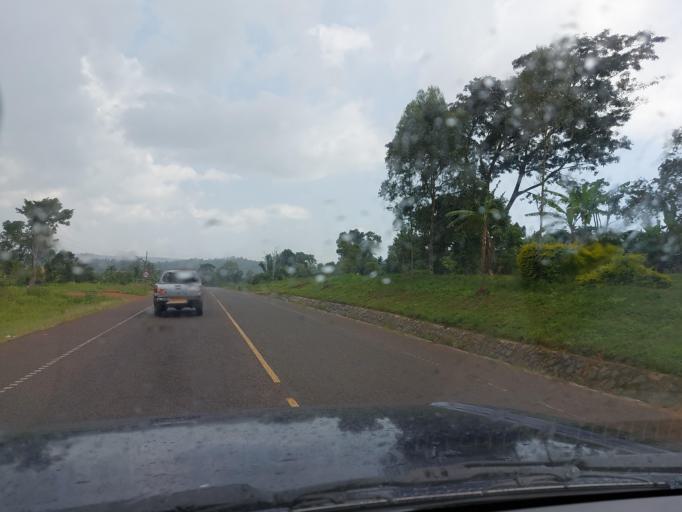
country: UG
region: Central Region
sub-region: Buikwe District
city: Buikwe
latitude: 0.2401
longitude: 32.9397
